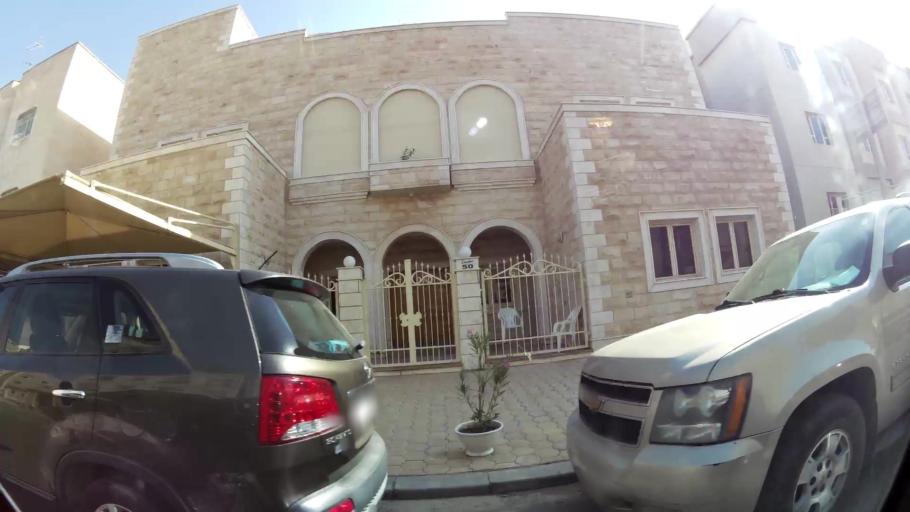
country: KW
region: Muhafazat Hawalli
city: Salwa
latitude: 29.2908
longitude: 48.0813
